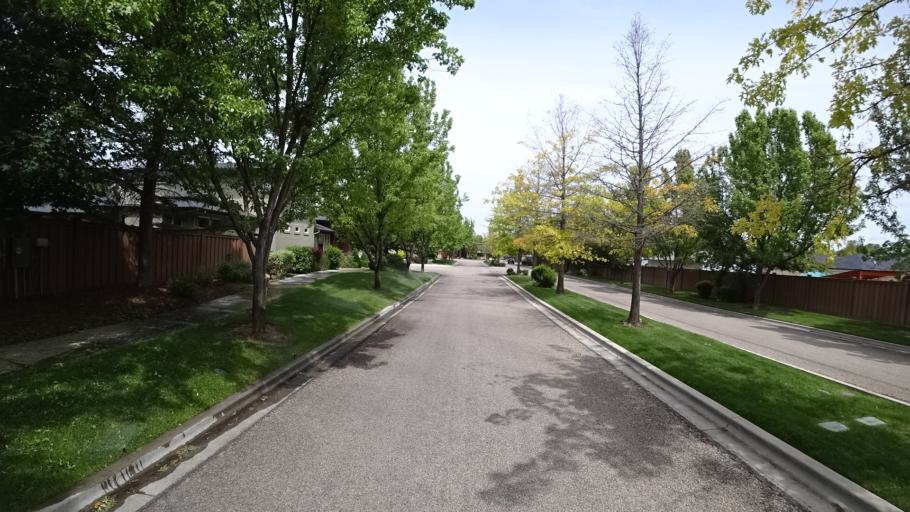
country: US
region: Idaho
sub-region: Ada County
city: Meridian
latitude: 43.5602
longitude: -116.3246
